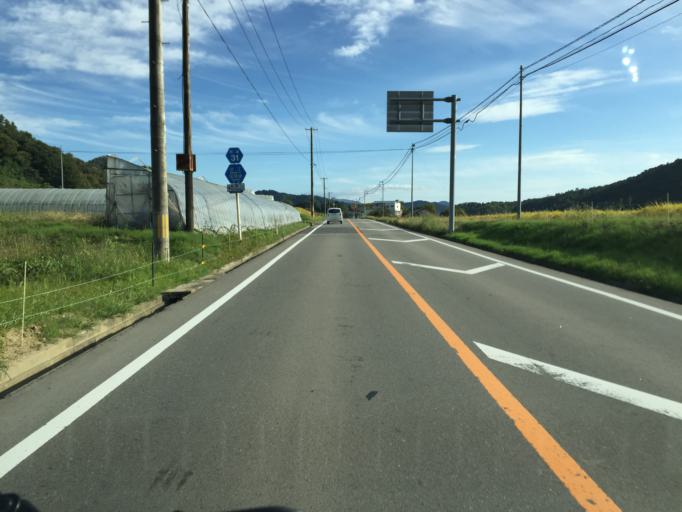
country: JP
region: Fukushima
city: Yanagawamachi-saiwaicho
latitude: 37.8107
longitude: 140.6187
